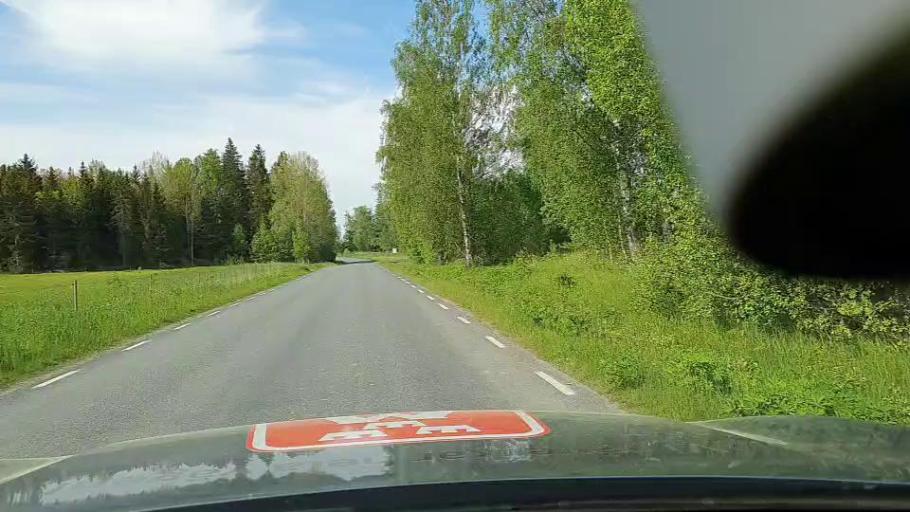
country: SE
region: Soedermanland
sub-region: Eskilstuna Kommun
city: Arla
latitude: 59.2725
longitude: 16.6648
